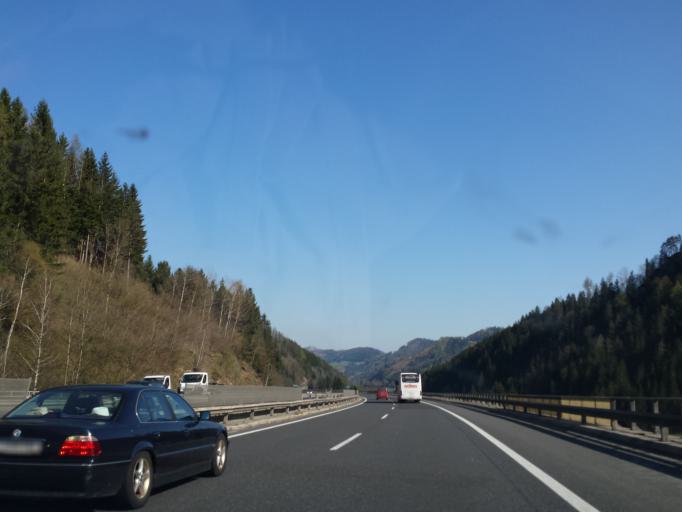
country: AT
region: Styria
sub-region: Politischer Bezirk Graz-Umgebung
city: Ubelbach
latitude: 47.2393
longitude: 15.1987
